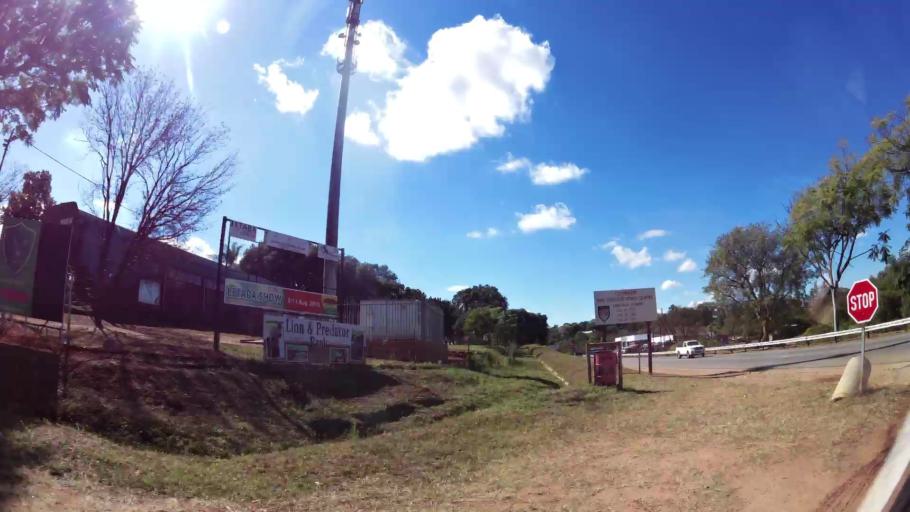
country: ZA
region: Limpopo
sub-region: Mopani District Municipality
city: Tzaneen
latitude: -23.8202
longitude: 30.1640
